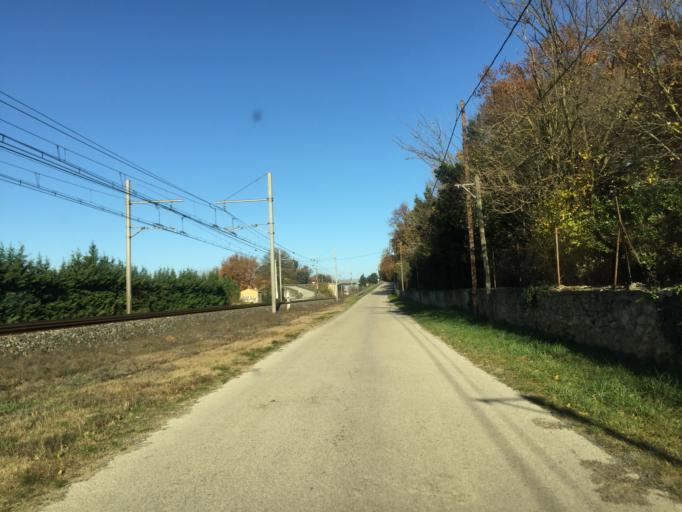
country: FR
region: Provence-Alpes-Cote d'Azur
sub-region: Departement du Vaucluse
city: Courthezon
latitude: 44.0669
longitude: 4.8919
